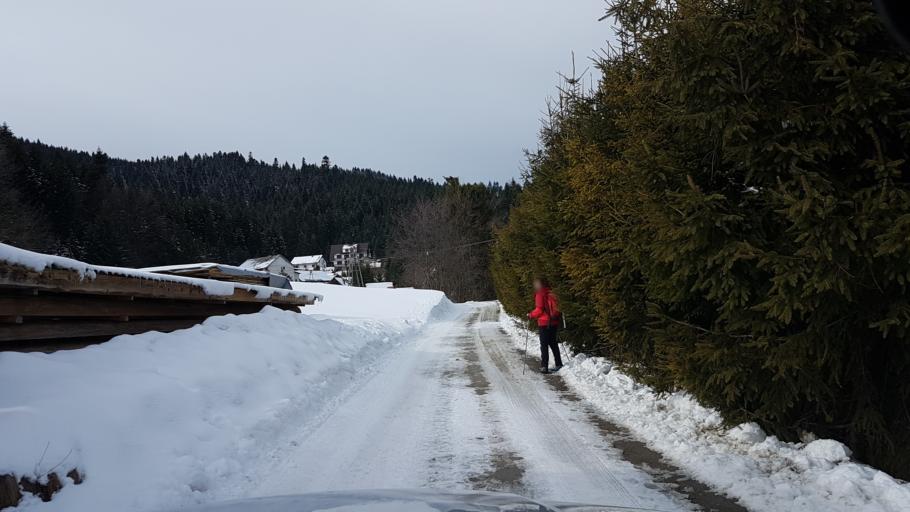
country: PL
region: Lesser Poland Voivodeship
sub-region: Powiat nowosadecki
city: Rytro
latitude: 49.4167
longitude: 20.6354
